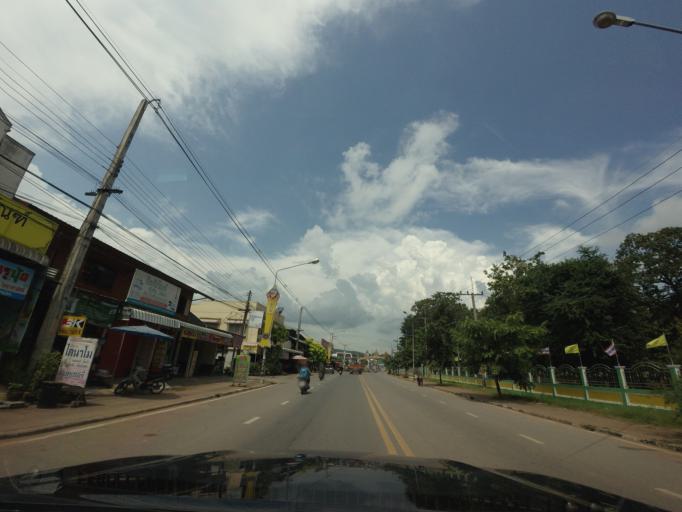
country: TH
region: Khon Kaen
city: Phu Wiang
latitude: 16.6559
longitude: 102.3730
